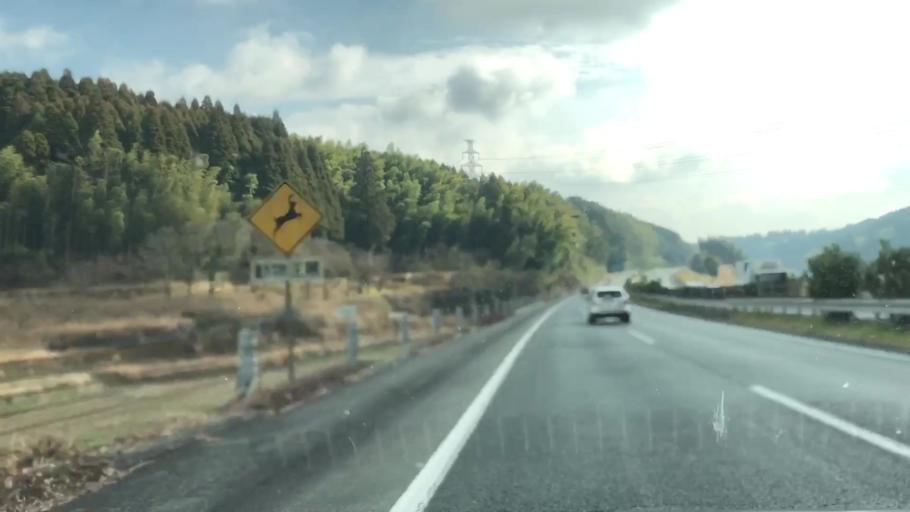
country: JP
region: Kumamoto
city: Yamaga
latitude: 33.0404
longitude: 130.5693
